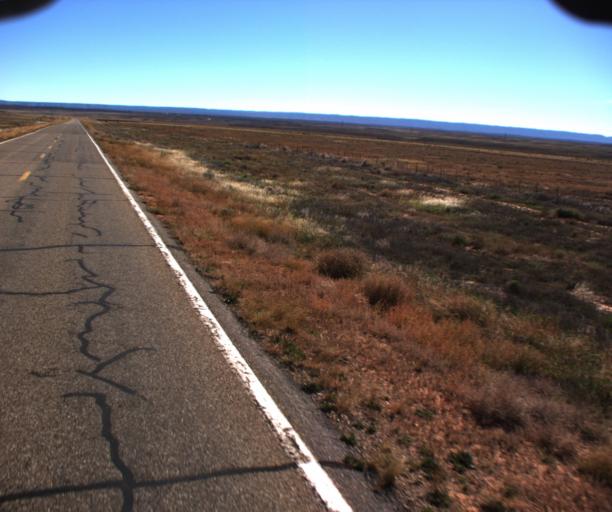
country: US
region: Arizona
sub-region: Coconino County
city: Fredonia
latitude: 36.9246
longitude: -112.4604
